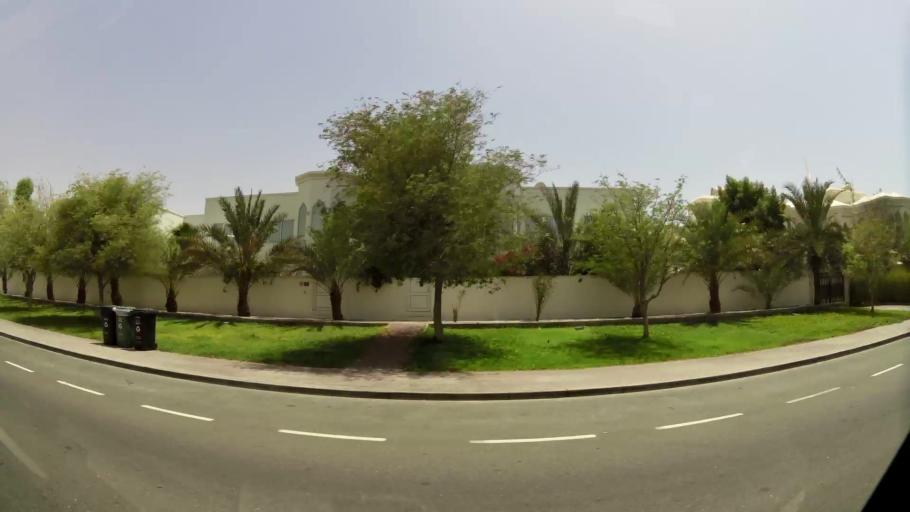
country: AE
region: Dubai
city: Dubai
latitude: 25.1425
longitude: 55.1955
